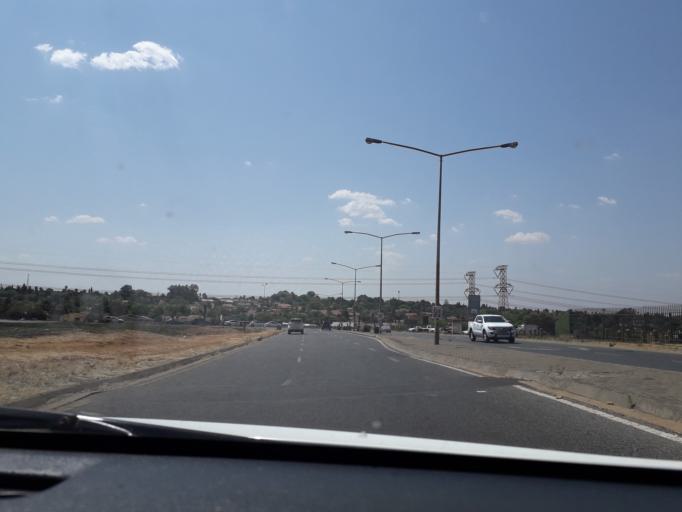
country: ZA
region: Gauteng
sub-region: City of Johannesburg Metropolitan Municipality
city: Modderfontein
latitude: -26.0892
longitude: 28.2004
